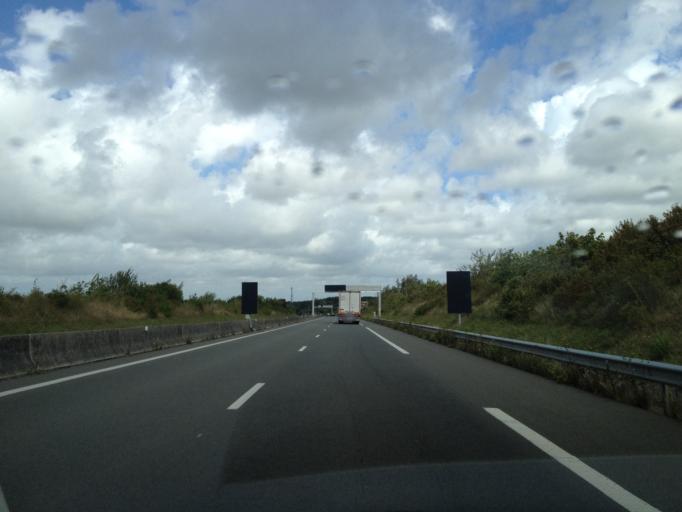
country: FR
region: Nord-Pas-de-Calais
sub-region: Departement du Pas-de-Calais
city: Nesles
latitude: 50.6267
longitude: 1.6623
